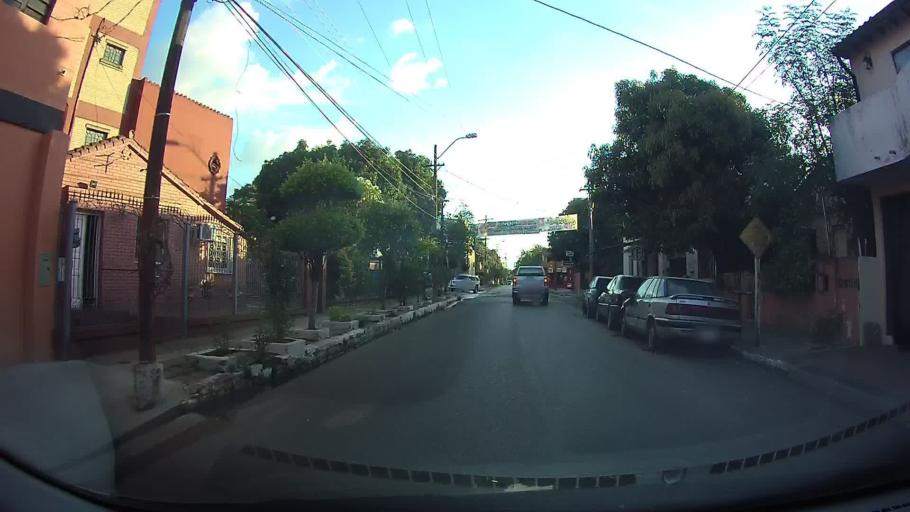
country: PY
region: Central
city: Fernando de la Mora
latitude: -25.3232
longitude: -57.5581
